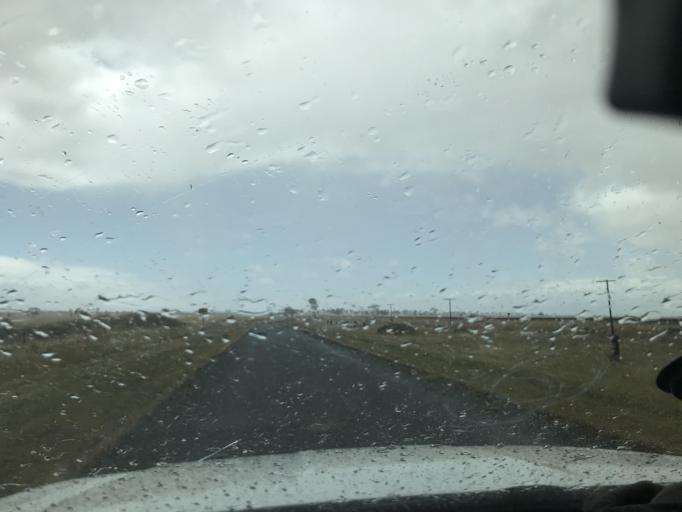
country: AU
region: South Australia
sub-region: Tatiara
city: Bordertown
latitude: -36.3750
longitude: 140.9947
